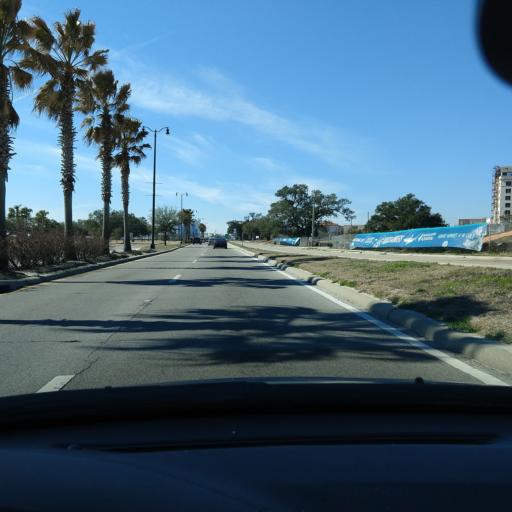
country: US
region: Mississippi
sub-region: Harrison County
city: Gulfport
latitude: 30.3674
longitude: -89.0879
